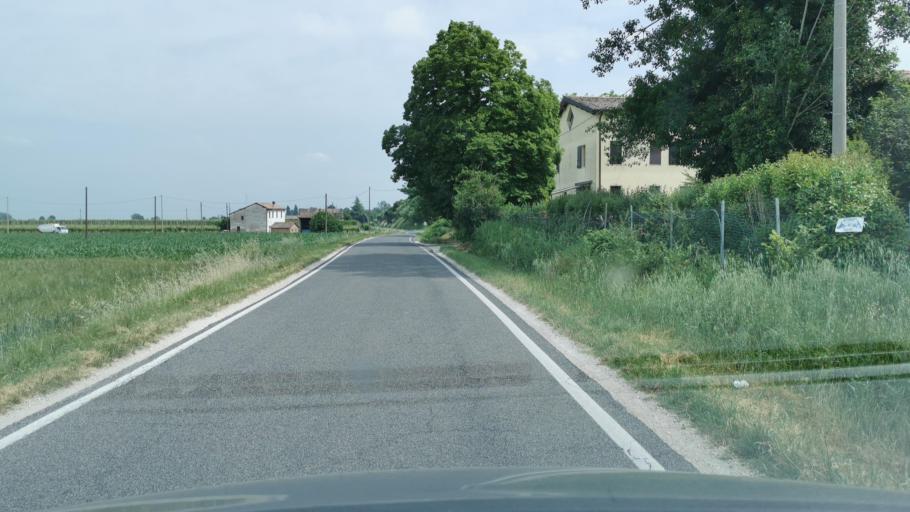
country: IT
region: Emilia-Romagna
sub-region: Provincia di Ravenna
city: Russi
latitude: 44.3912
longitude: 12.0125
